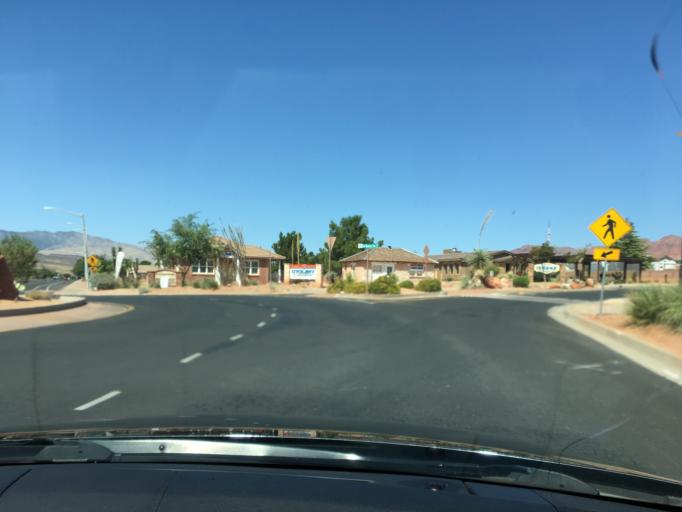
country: US
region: Utah
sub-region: Washington County
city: Ivins
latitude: 37.1685
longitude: -113.6746
